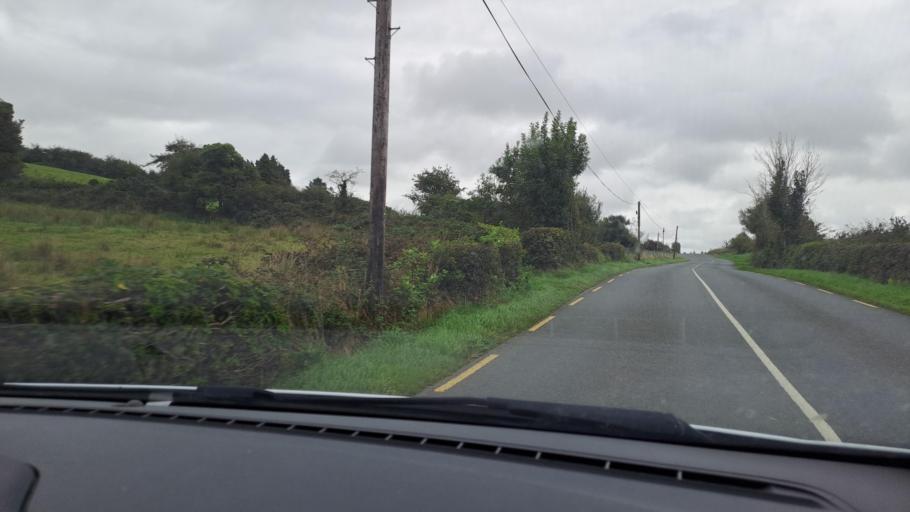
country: IE
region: Ulster
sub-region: County Monaghan
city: Carrickmacross
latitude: 54.0371
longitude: -6.7868
